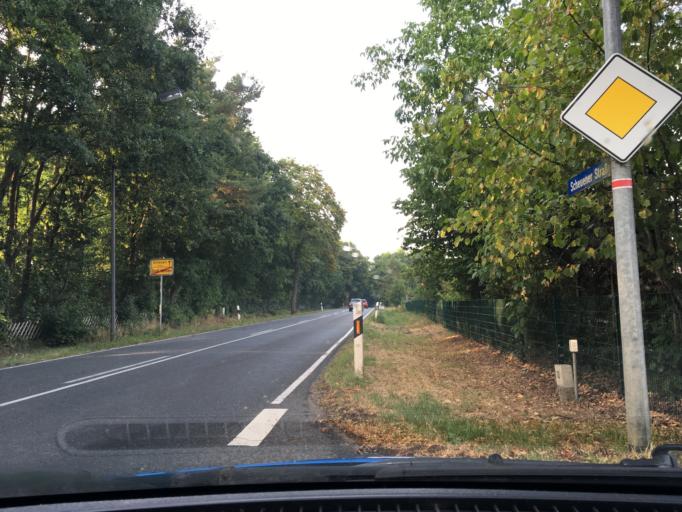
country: DE
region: Lower Saxony
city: Celle
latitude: 52.6601
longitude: 10.0675
